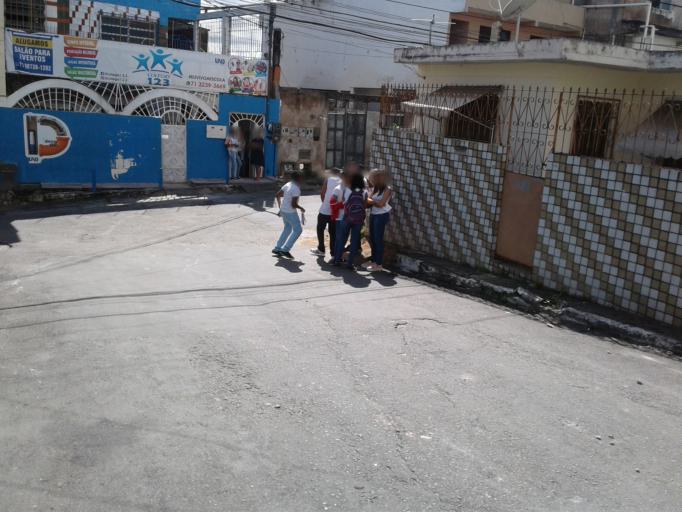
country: BR
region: Bahia
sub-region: Salvador
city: Salvador
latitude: -12.9124
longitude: -38.4699
